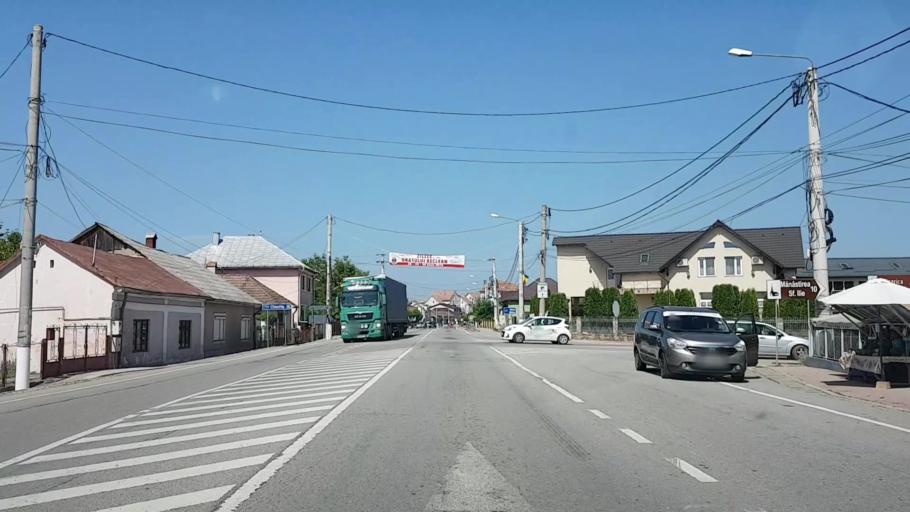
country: RO
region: Bistrita-Nasaud
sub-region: Comuna Beclean
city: Beclean
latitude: 47.1755
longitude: 24.1701
